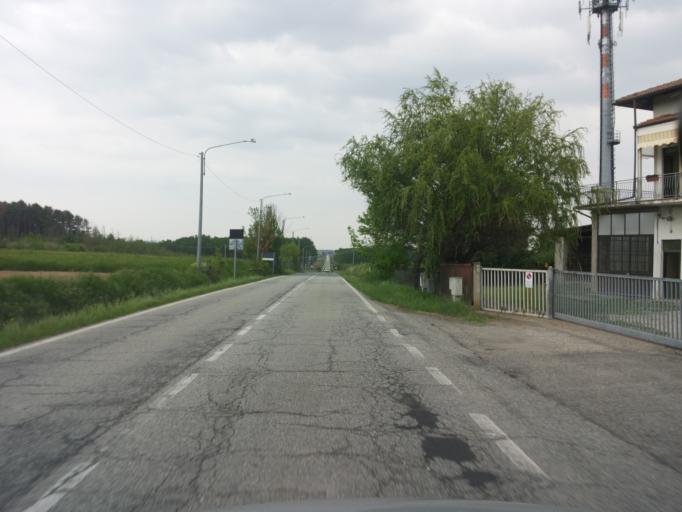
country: IT
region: Piedmont
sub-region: Provincia di Alessandria
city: Mirabello Monferrato
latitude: 45.0393
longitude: 8.5248
